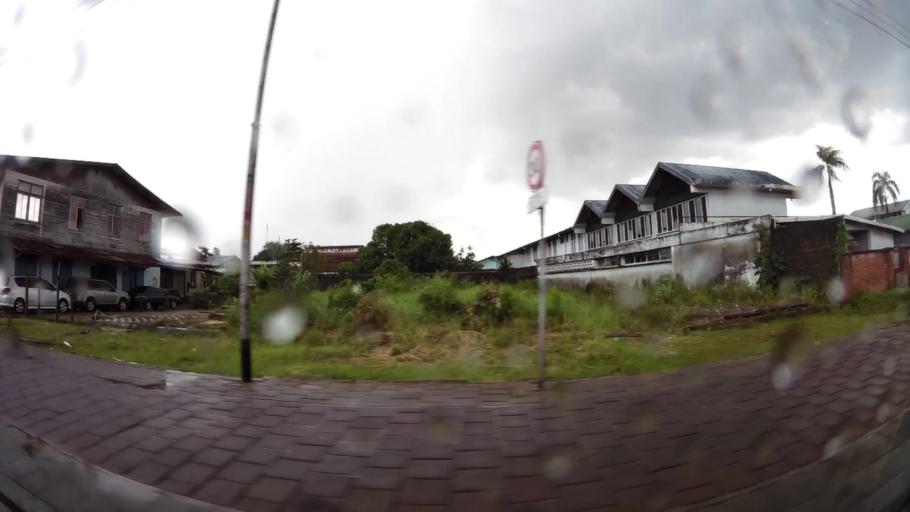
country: SR
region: Paramaribo
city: Paramaribo
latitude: 5.8239
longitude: -55.1718
